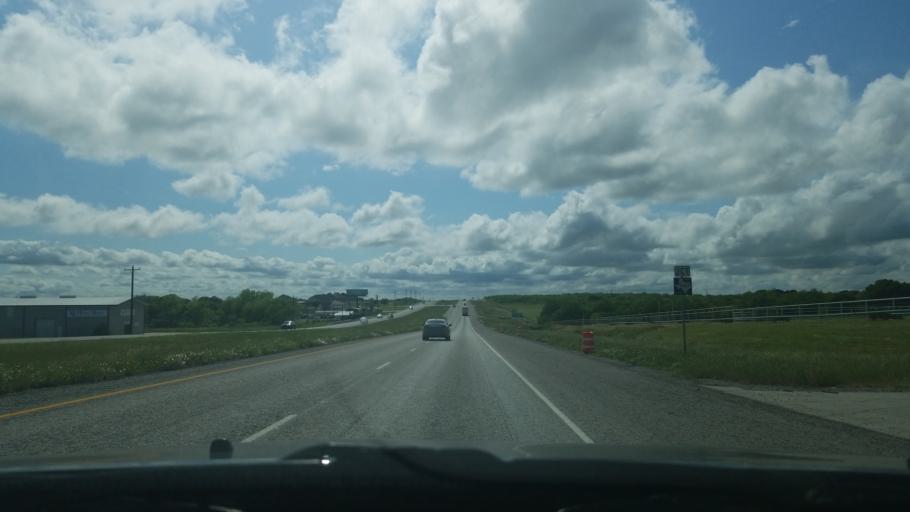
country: US
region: Texas
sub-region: Denton County
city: Ponder
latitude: 33.2407
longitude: -97.3497
